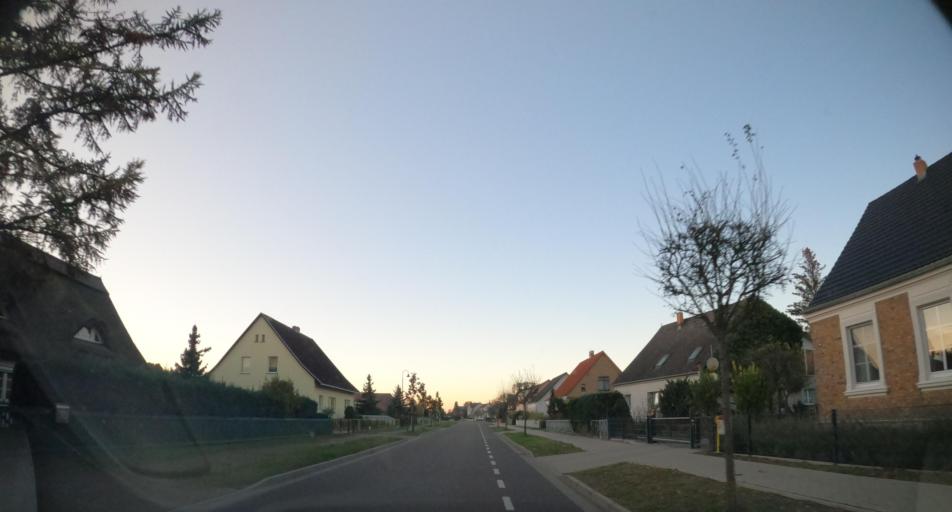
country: DE
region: Mecklenburg-Vorpommern
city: Ueckermunde
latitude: 53.7575
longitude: 14.0139
